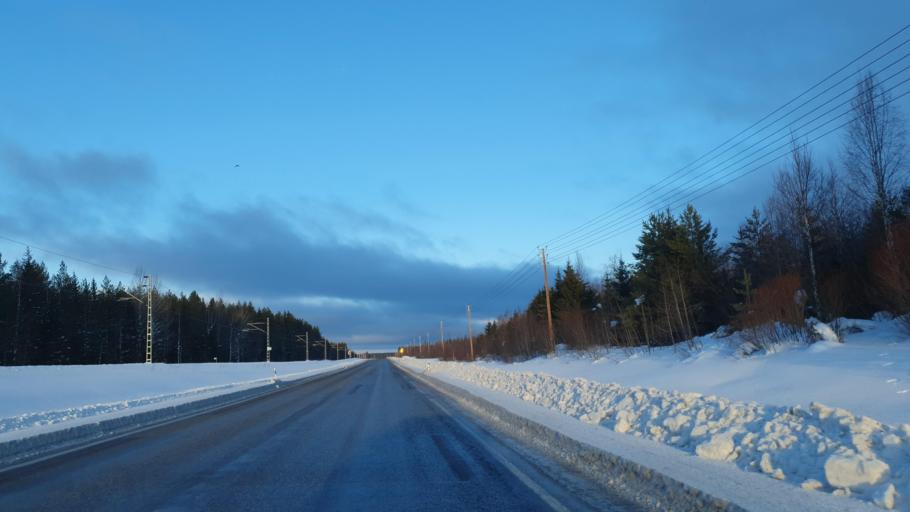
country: FI
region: Kainuu
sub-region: Kajaani
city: Paltamo
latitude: 64.4100
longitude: 27.7572
